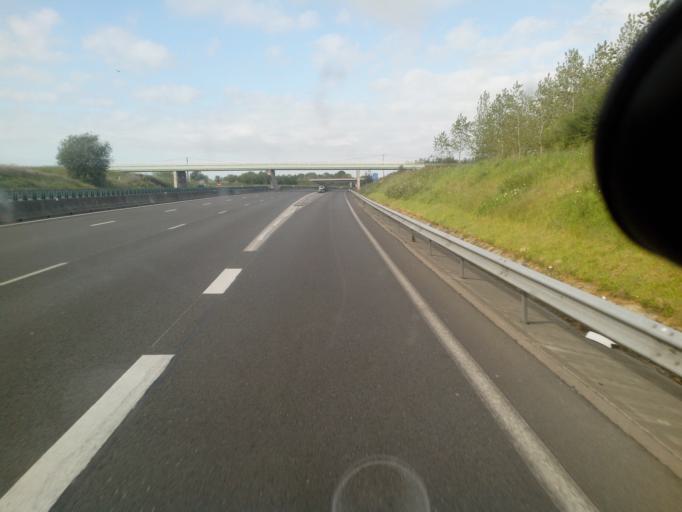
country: FR
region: Haute-Normandie
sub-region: Departement de l'Eure
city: Beuzeville
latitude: 49.3160
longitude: 0.3088
